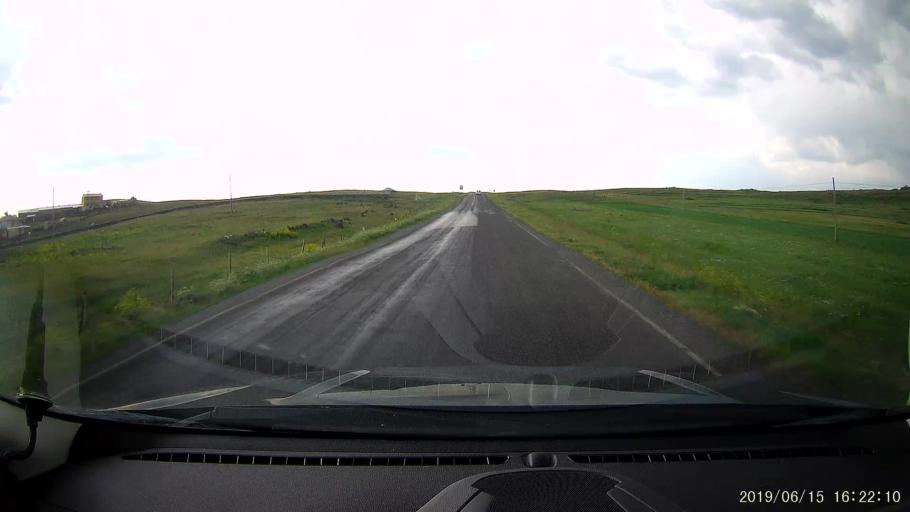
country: TR
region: Ardahan
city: Hanak
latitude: 41.1907
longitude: 42.8478
